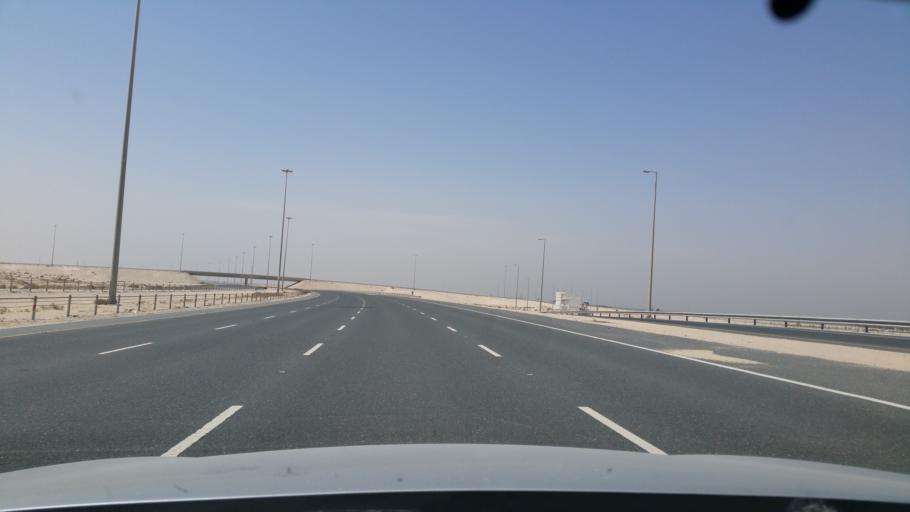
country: QA
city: Umm Bab
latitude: 24.8429
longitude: 50.8744
